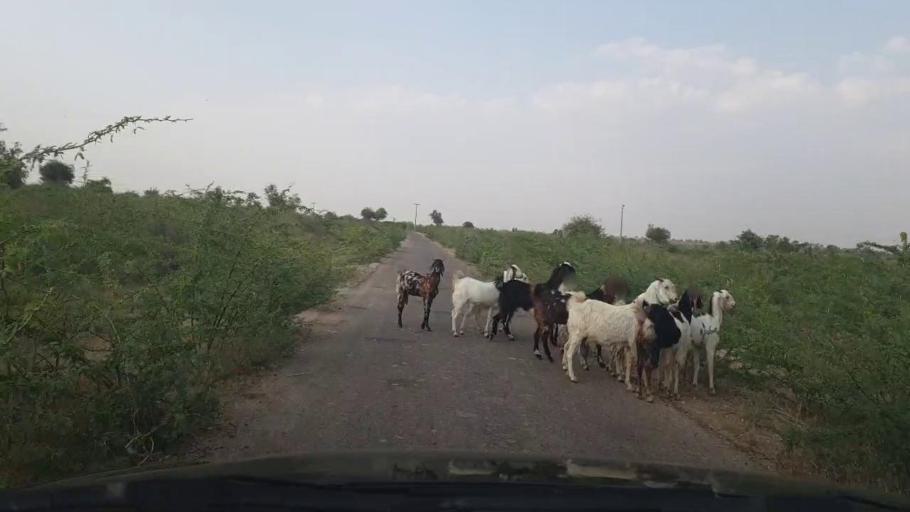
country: PK
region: Sindh
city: Islamkot
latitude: 25.0388
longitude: 70.5557
